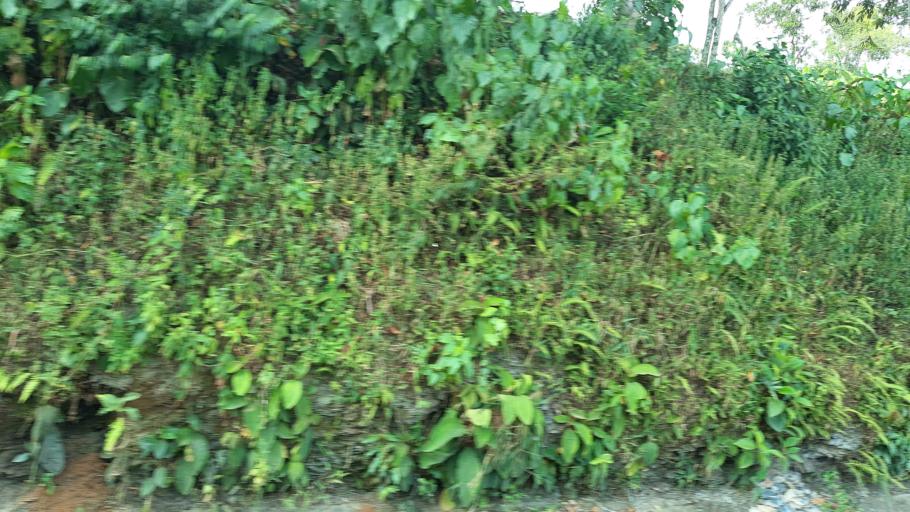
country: CO
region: Boyaca
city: Moniquira
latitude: 5.8416
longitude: -73.5861
